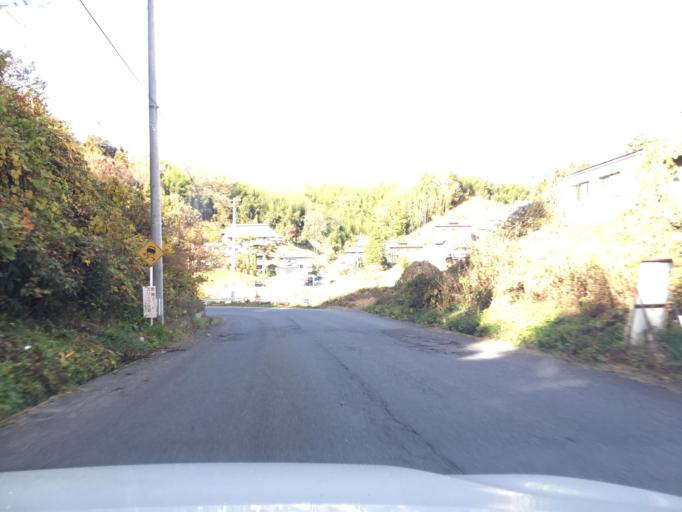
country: JP
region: Fukushima
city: Miharu
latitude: 37.4597
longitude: 140.4997
